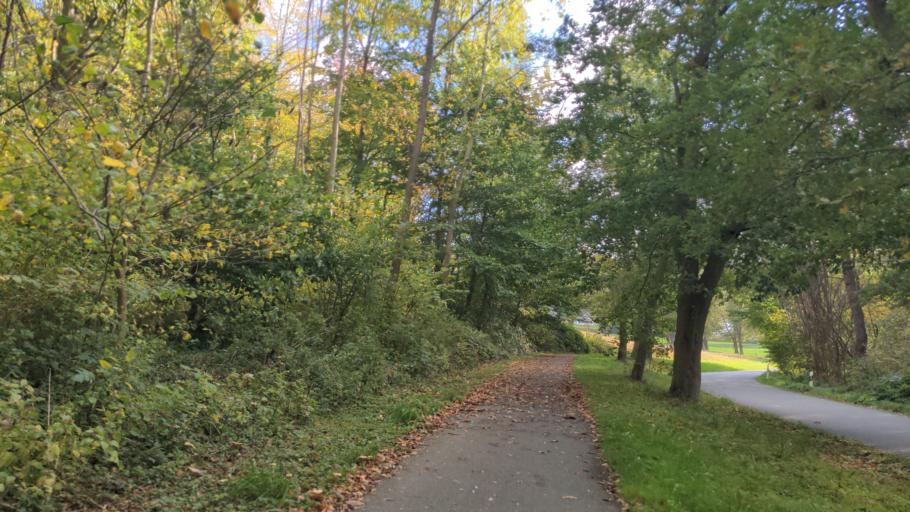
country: DE
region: Schleswig-Holstein
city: Bosau
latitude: 54.1226
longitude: 10.4458
